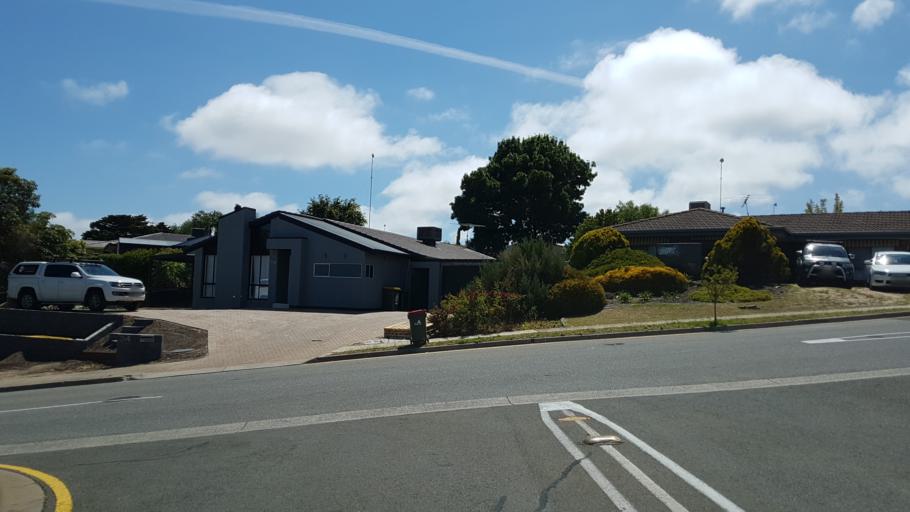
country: AU
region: South Australia
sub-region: Marion
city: Happy Valley
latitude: -35.0703
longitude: 138.5153
